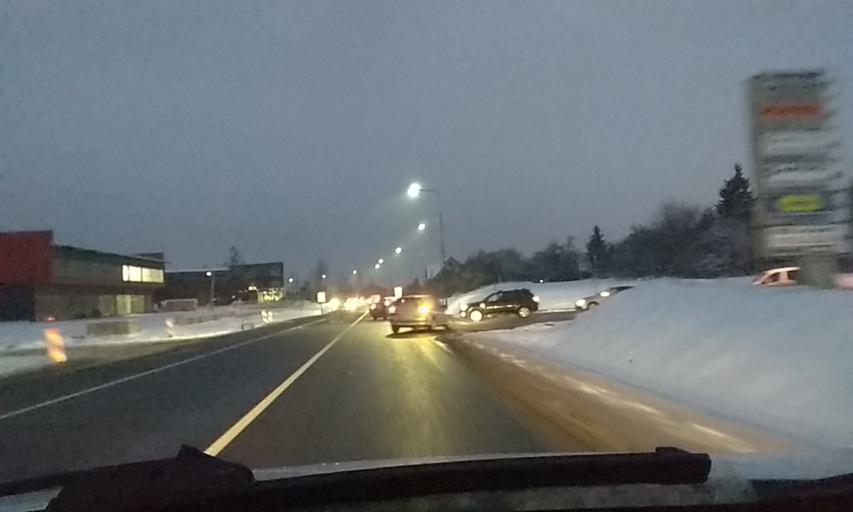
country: LT
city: Ramuciai
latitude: 54.9028
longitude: 24.0247
